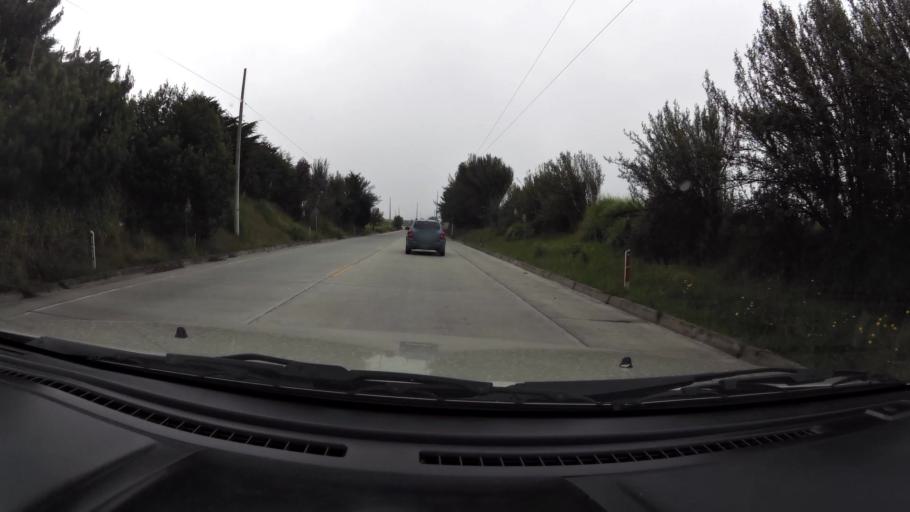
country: EC
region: Canar
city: Canar
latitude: -2.5876
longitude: -78.9180
